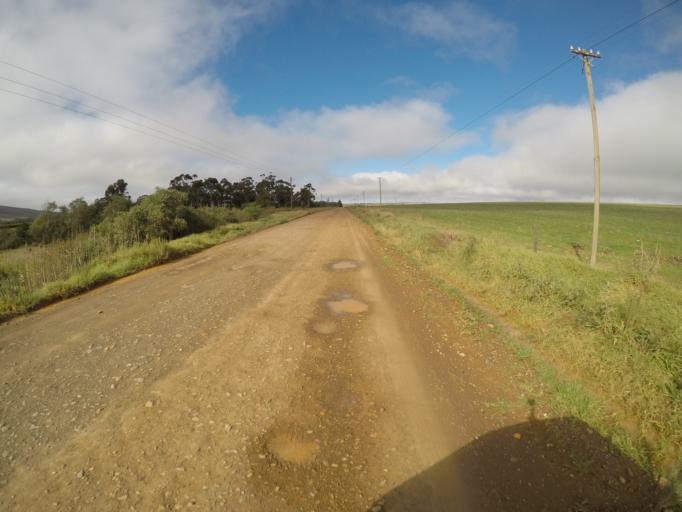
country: ZA
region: Western Cape
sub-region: Cape Winelands District Municipality
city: Ashton
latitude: -34.1372
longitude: 19.8595
